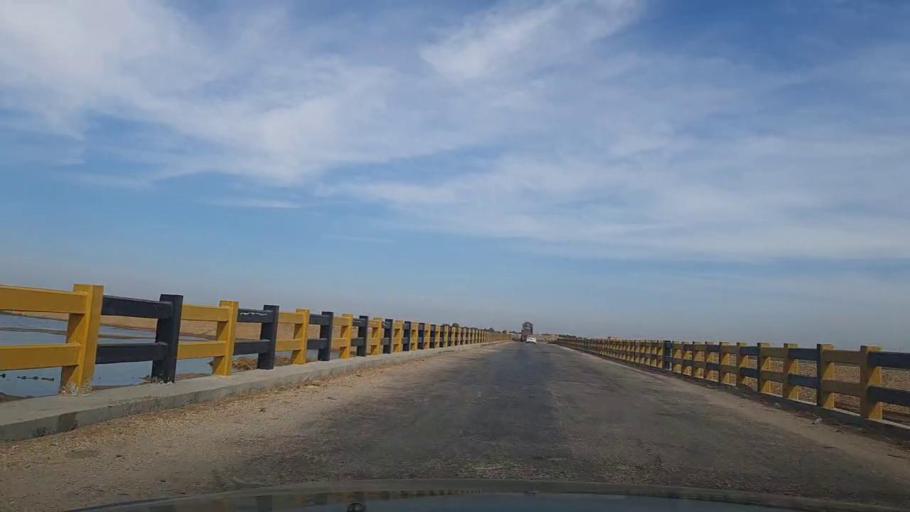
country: PK
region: Sindh
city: Daro Mehar
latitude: 24.9039
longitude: 68.0686
